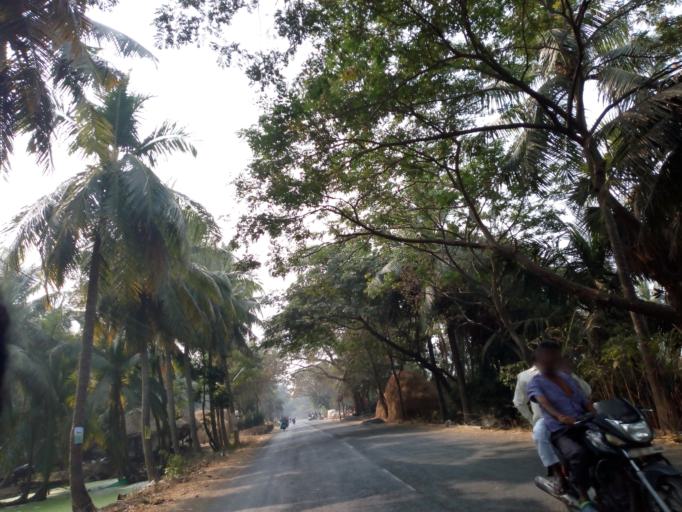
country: IN
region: Andhra Pradesh
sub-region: West Godavari
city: Akividu
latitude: 16.6130
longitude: 81.4634
